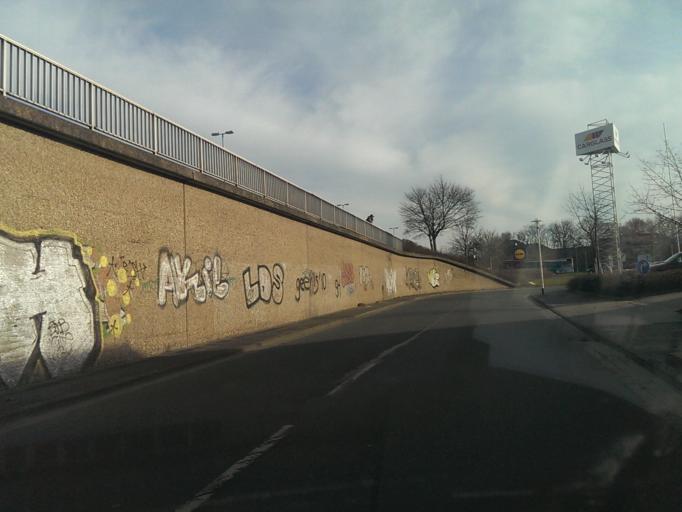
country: DE
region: Lower Saxony
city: Hildesheim
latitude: 52.1624
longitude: 9.9624
